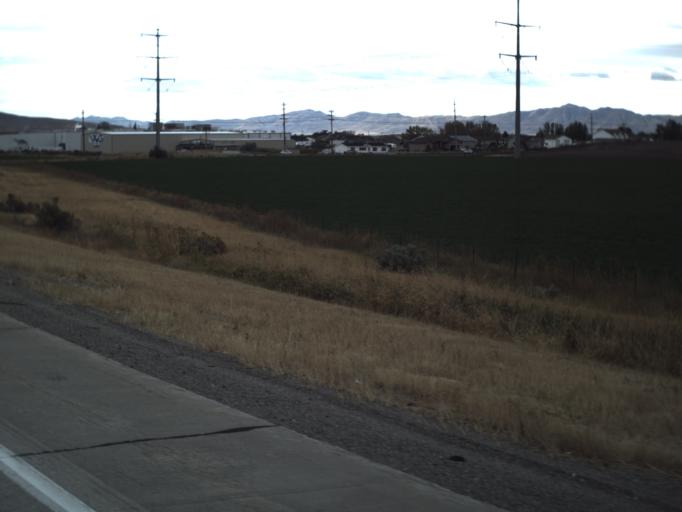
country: US
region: Utah
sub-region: Box Elder County
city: Tremonton
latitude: 41.7291
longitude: -112.1931
